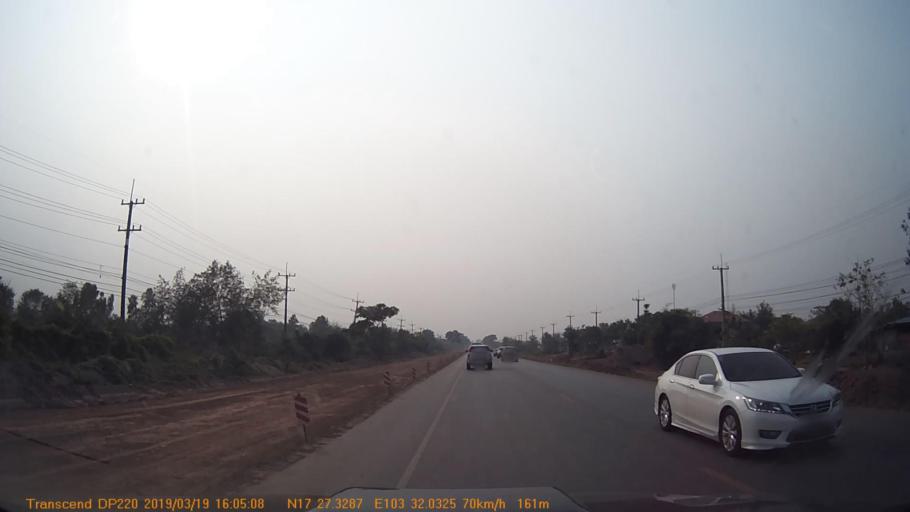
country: TH
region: Sakon Nakhon
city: Sawang Daen Din
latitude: 17.4555
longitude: 103.5337
